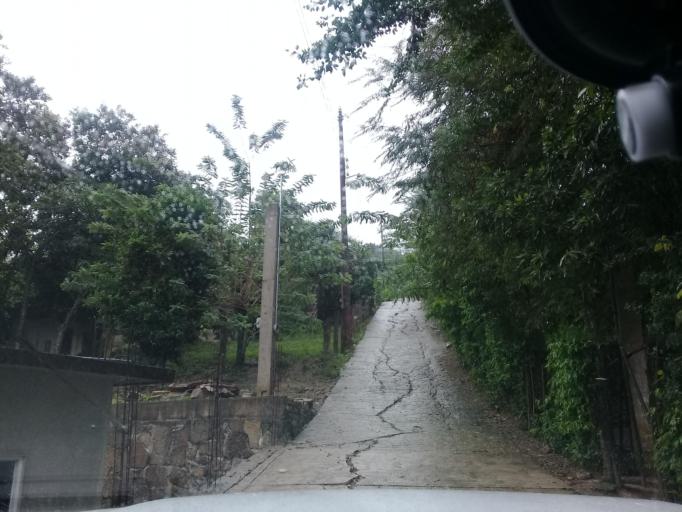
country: MX
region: Veracruz
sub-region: Chalma
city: San Pedro Coyutla
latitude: 21.2296
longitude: -98.4448
